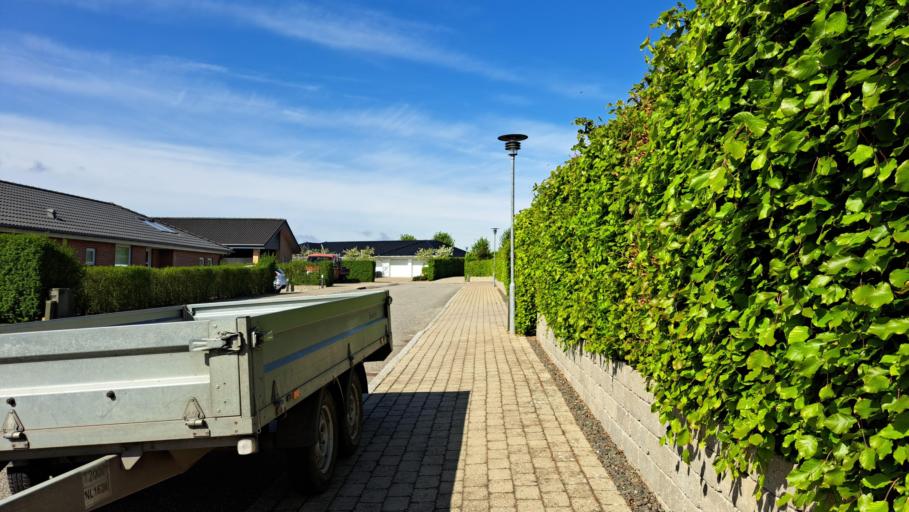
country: DK
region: Central Jutland
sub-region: Hedensted Kommune
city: Hedensted
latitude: 55.8008
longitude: 9.6472
